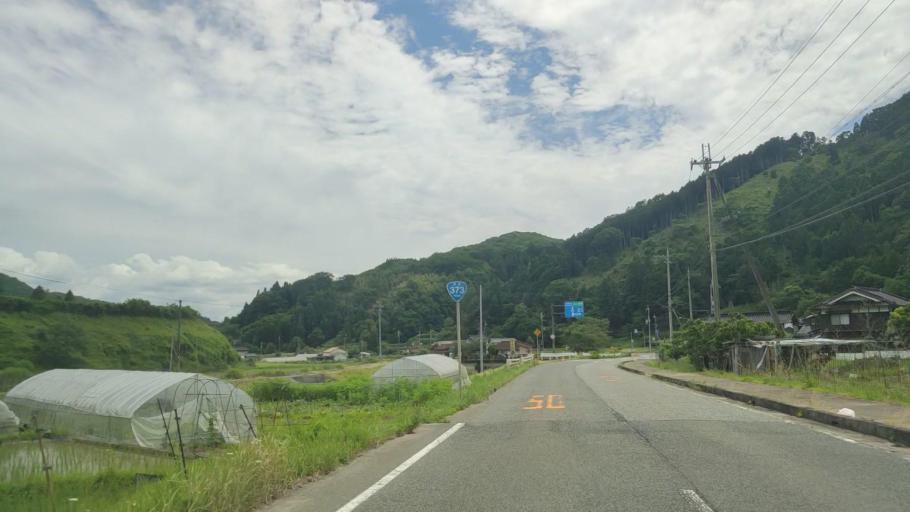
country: JP
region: Hyogo
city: Yamazakicho-nakabirose
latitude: 35.0544
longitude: 134.3659
